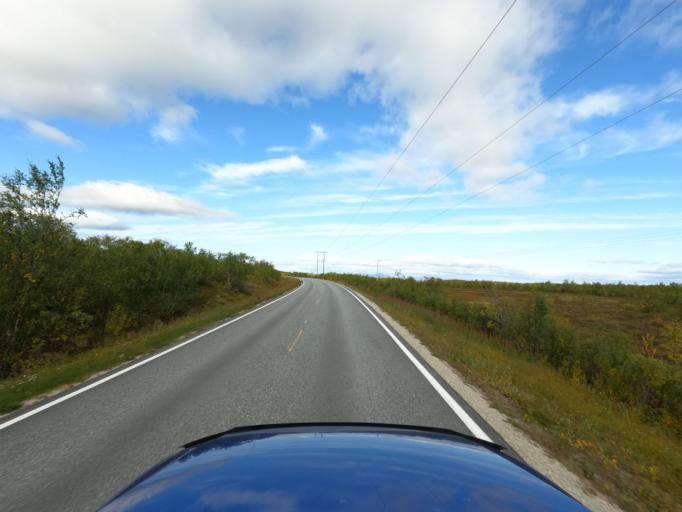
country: NO
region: Finnmark Fylke
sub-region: Karasjok
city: Karasjohka
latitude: 69.6639
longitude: 25.2761
